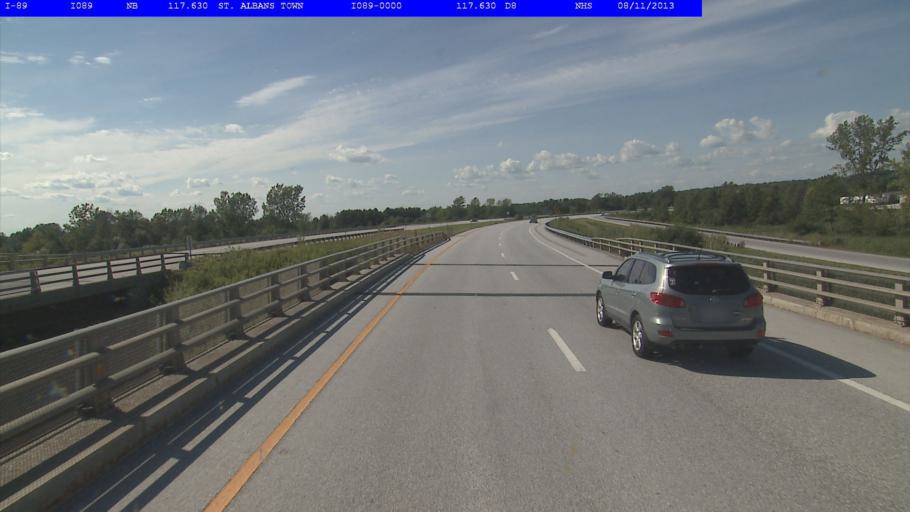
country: US
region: Vermont
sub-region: Franklin County
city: Saint Albans
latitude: 44.8437
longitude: -73.0795
